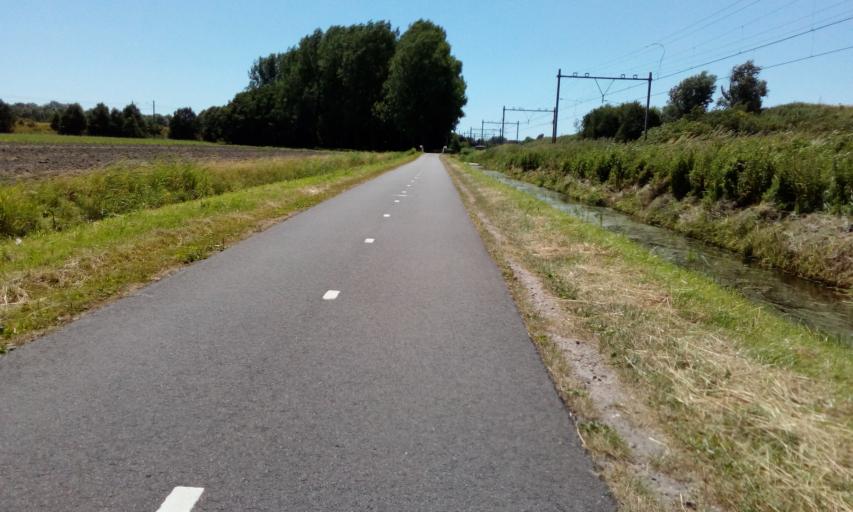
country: NL
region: South Holland
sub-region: Gemeente Teylingen
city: Voorhout
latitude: 52.2041
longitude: 4.4918
